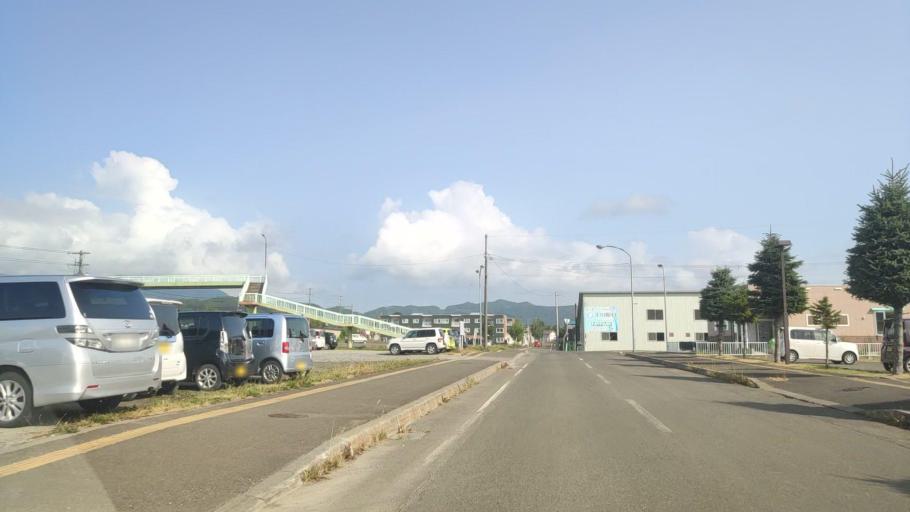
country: JP
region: Hokkaido
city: Shimo-furano
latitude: 43.3487
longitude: 142.3916
